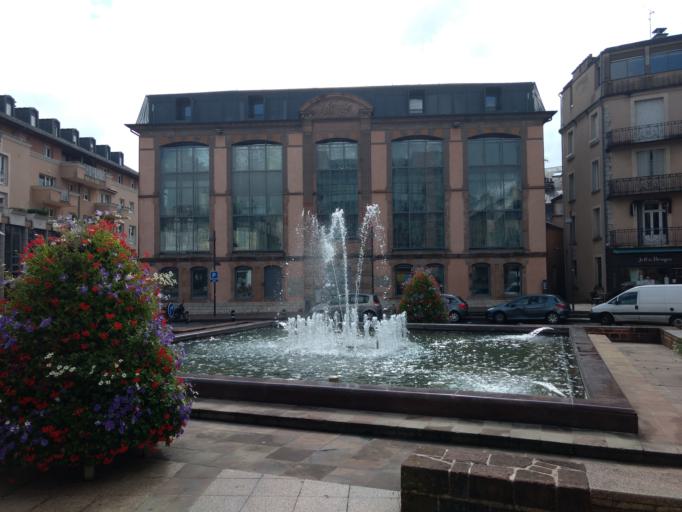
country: FR
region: Midi-Pyrenees
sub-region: Departement de l'Aveyron
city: Rodez
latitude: 44.3494
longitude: 2.5766
